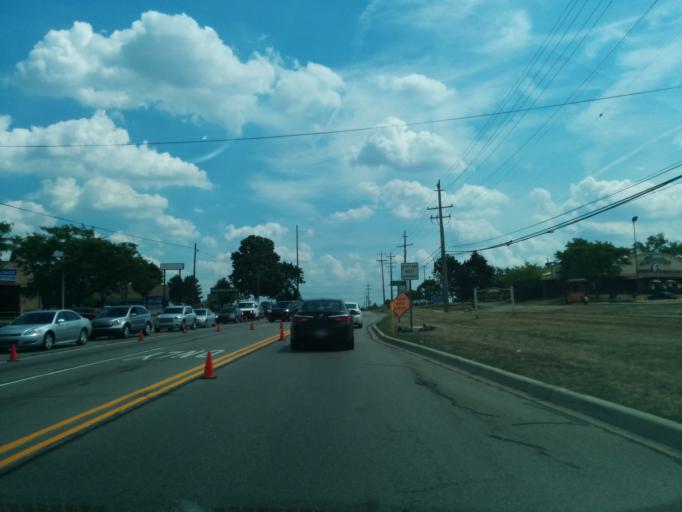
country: US
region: Michigan
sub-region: Oakland County
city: Novi
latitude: 42.4717
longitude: -83.4348
